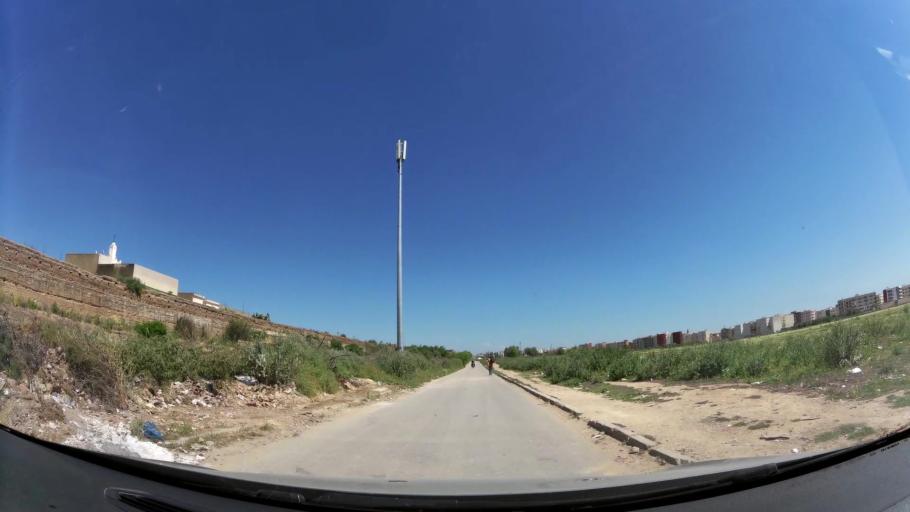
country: MA
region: Meknes-Tafilalet
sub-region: Meknes
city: Meknes
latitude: 33.8654
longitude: -5.5575
